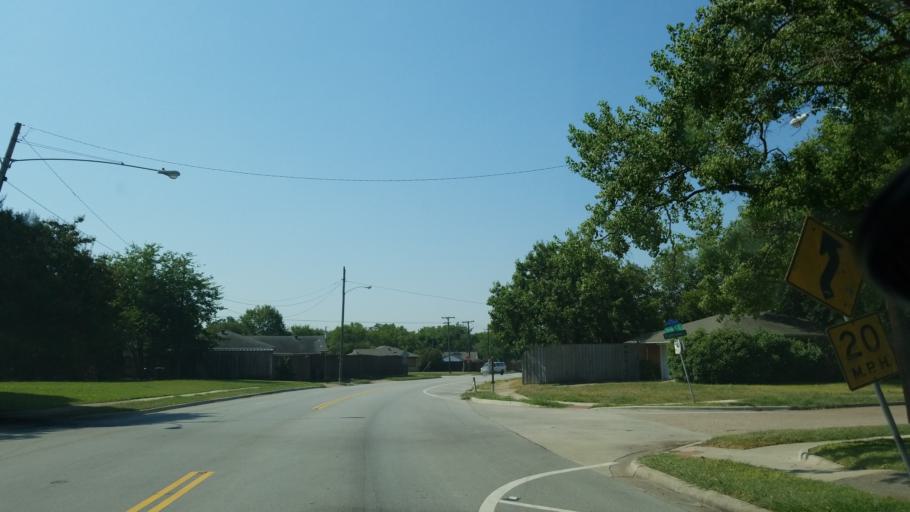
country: US
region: Texas
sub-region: Dallas County
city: Richardson
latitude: 32.8727
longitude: -96.7086
